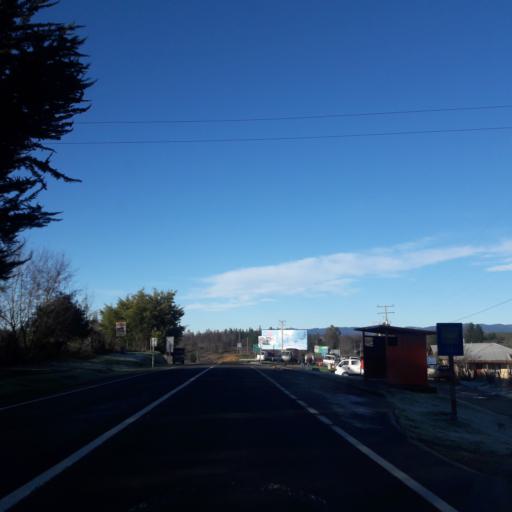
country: CL
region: Biobio
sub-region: Provincia de Biobio
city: La Laja
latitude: -37.3163
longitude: -72.9221
